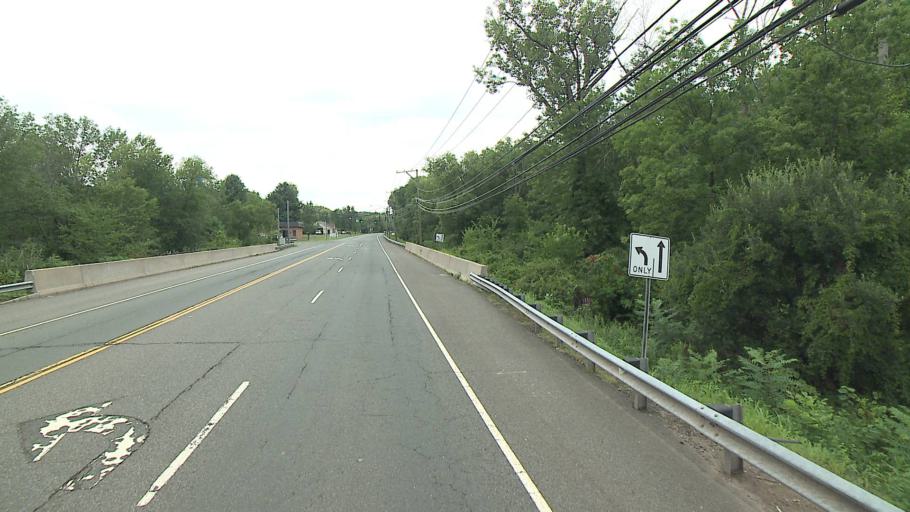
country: US
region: Connecticut
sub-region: Middlesex County
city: Cromwell
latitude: 41.5937
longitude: -72.6764
